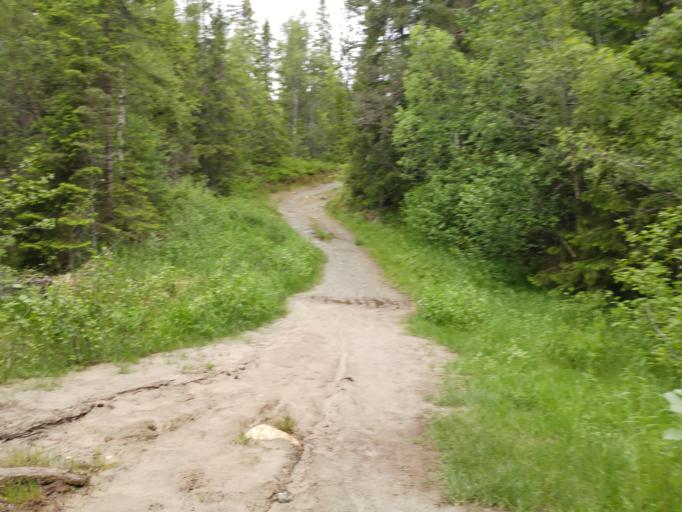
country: NO
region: Sor-Trondelag
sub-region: Melhus
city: Melhus
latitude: 63.3904
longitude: 10.2854
